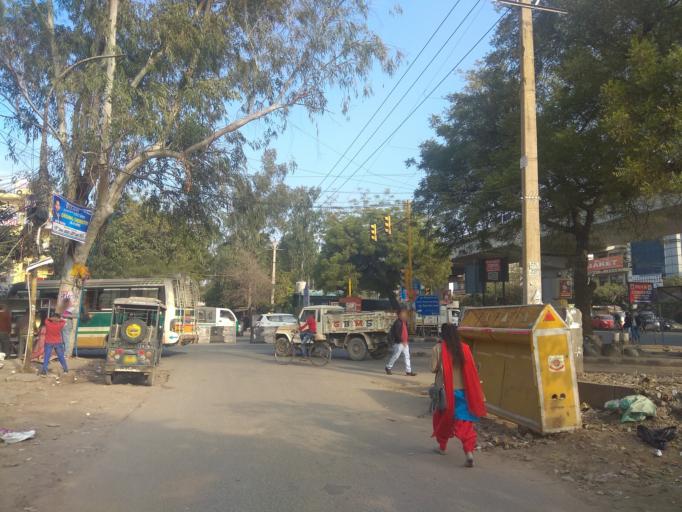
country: IN
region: NCT
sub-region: West Delhi
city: Nangloi Jat
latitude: 28.6269
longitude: 77.0698
